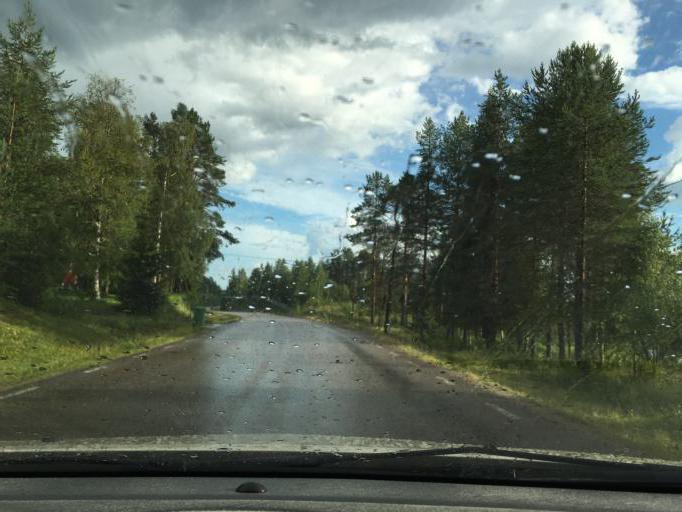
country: SE
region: Norrbotten
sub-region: Kalix Kommun
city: Rolfs
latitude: 65.9384
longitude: 22.8920
